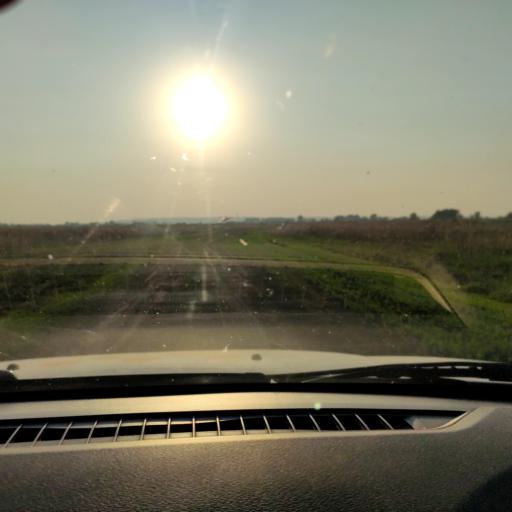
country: RU
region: Bashkortostan
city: Mikhaylovka
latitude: 54.9533
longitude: 55.8160
